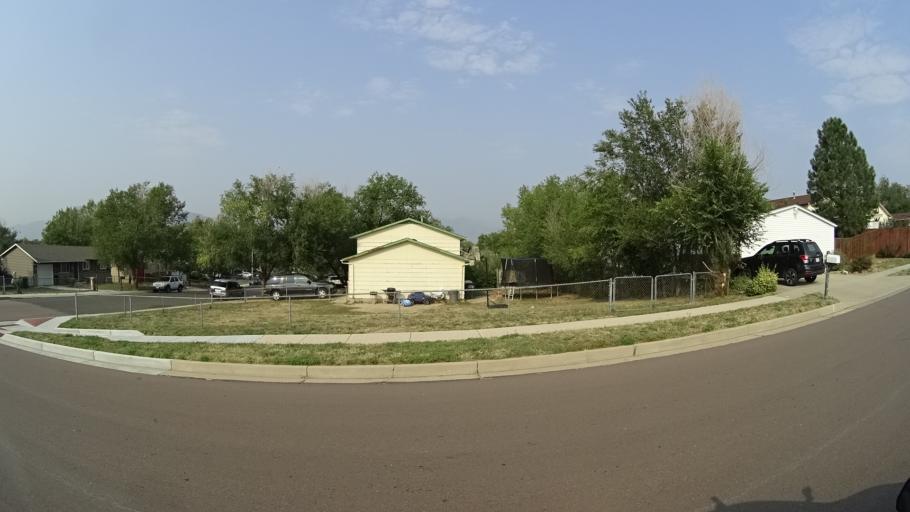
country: US
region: Colorado
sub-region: El Paso County
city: Stratmoor
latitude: 38.8084
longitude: -104.7593
